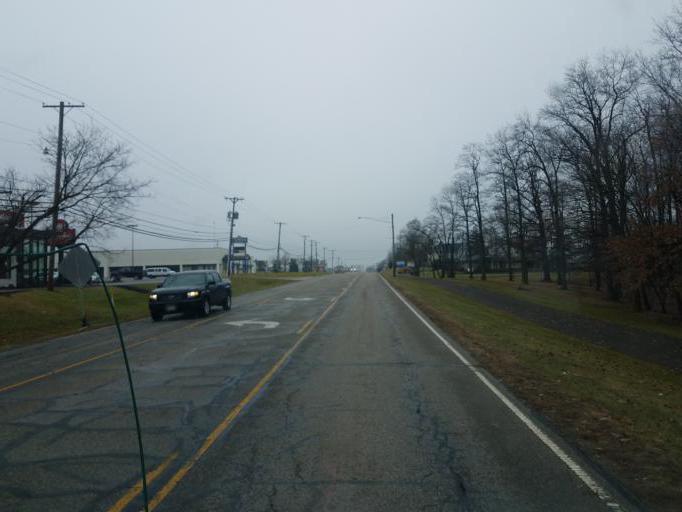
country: US
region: Ohio
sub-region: Union County
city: Marysville
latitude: 40.2399
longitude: -83.3863
